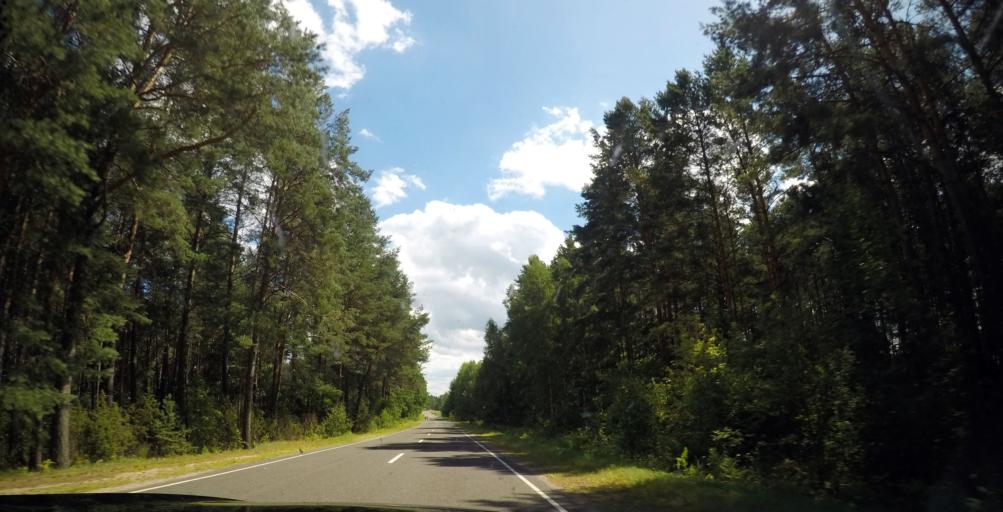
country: LT
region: Alytaus apskritis
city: Druskininkai
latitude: 53.8729
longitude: 24.1552
